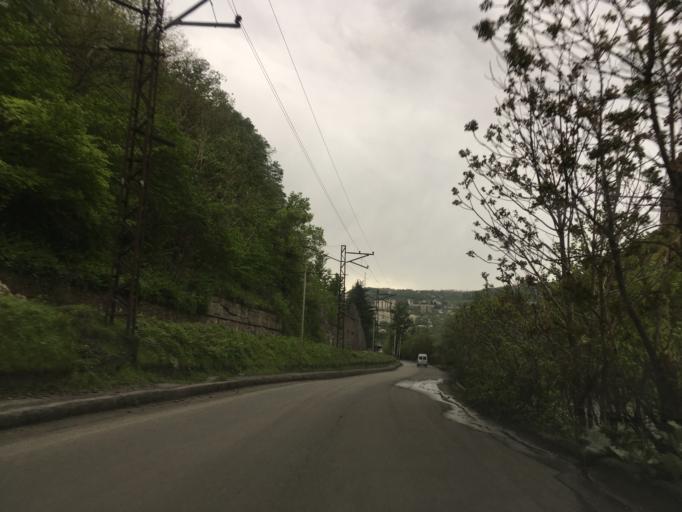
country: GE
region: Racha-Lechkhumi and Kvemo Svaneti
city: Gori
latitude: 42.2906
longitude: 43.2961
